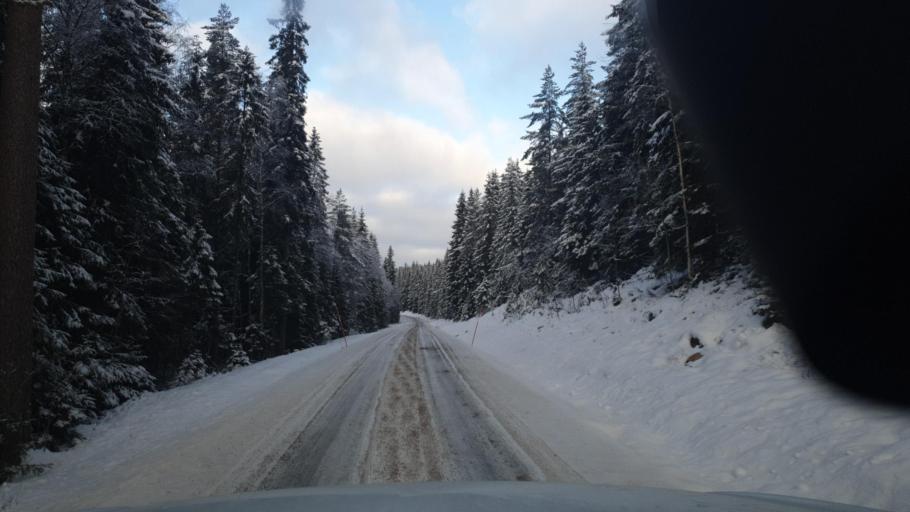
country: SE
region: Vaermland
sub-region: Eda Kommun
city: Charlottenberg
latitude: 60.0786
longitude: 12.6197
